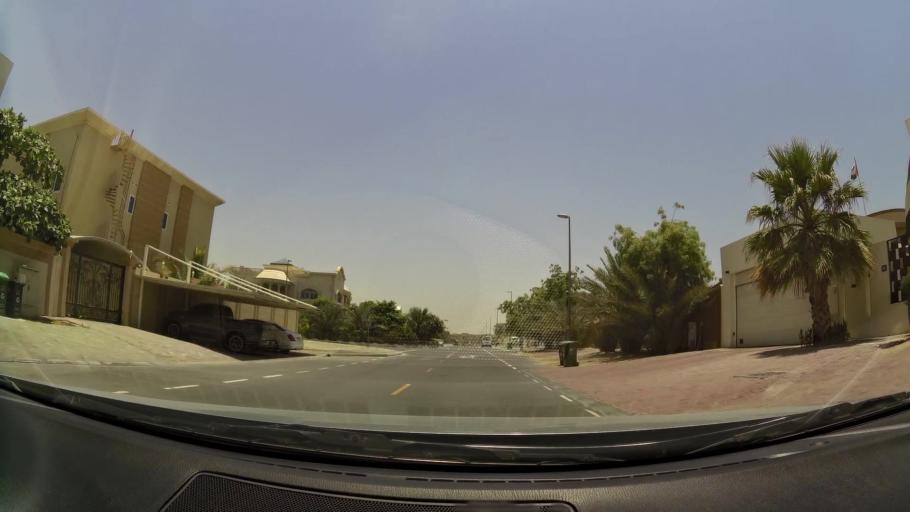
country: AE
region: Dubai
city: Dubai
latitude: 25.0981
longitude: 55.1887
